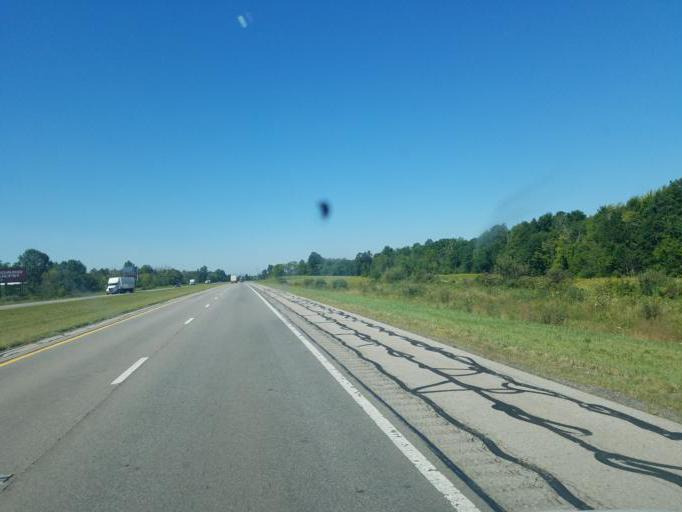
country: US
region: Ohio
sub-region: Crawford County
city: Crestline
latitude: 40.7667
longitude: -82.6836
